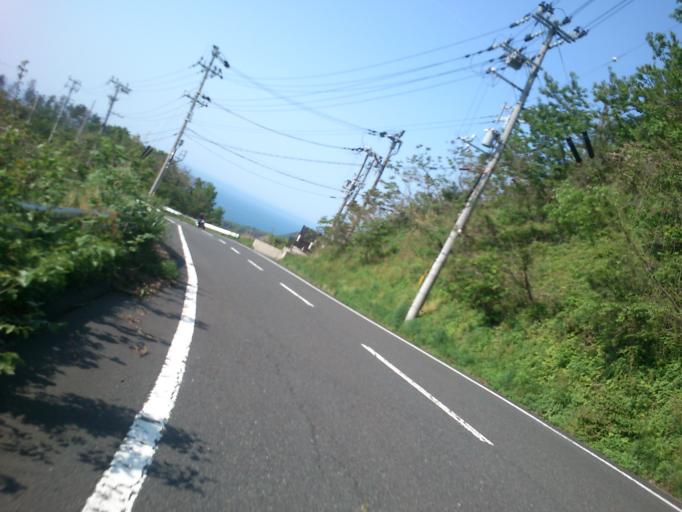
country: JP
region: Kyoto
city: Miyazu
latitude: 35.7368
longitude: 135.1758
